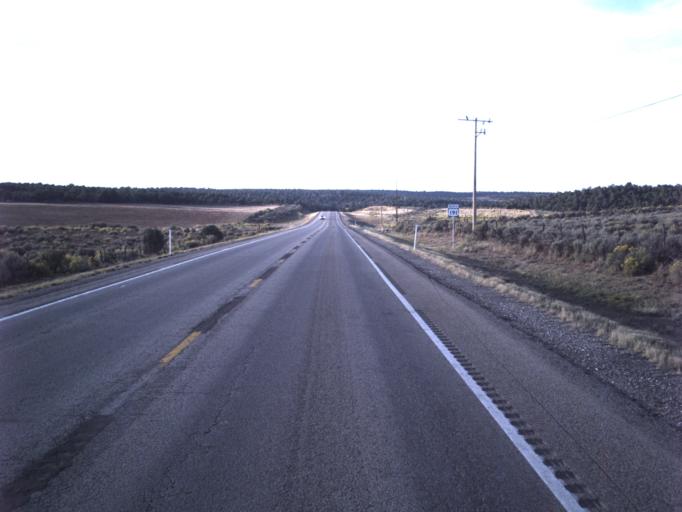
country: US
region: Utah
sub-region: San Juan County
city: Monticello
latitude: 37.9585
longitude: -109.3520
